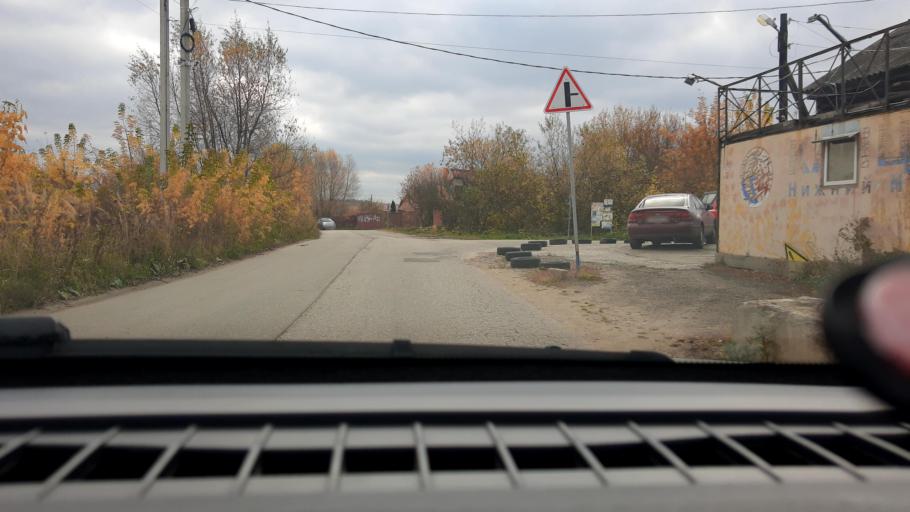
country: RU
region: Nizjnij Novgorod
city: Afonino
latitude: 56.2013
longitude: 44.0957
